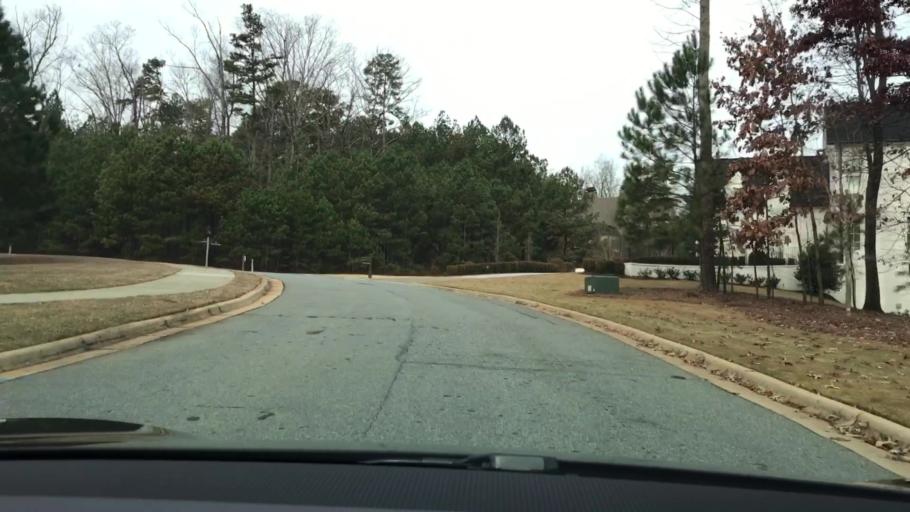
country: US
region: Georgia
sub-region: Gwinnett County
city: Suwanee
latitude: 34.0746
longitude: -84.1067
